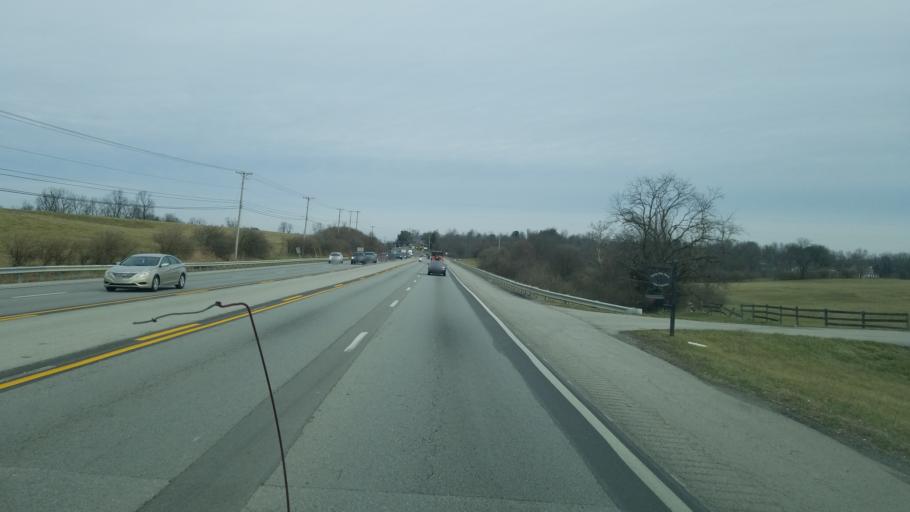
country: US
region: Kentucky
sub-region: Fayette County
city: Monticello
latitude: 37.9597
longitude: -84.5373
